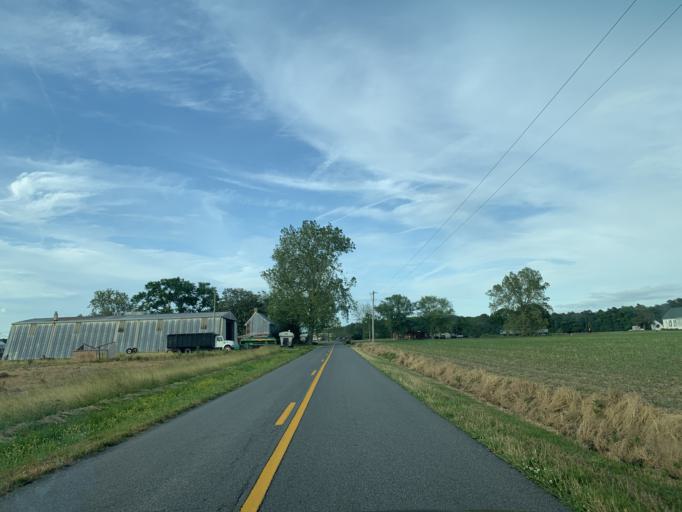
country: US
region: Maryland
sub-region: Worcester County
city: Snow Hill
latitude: 38.0965
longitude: -75.4564
